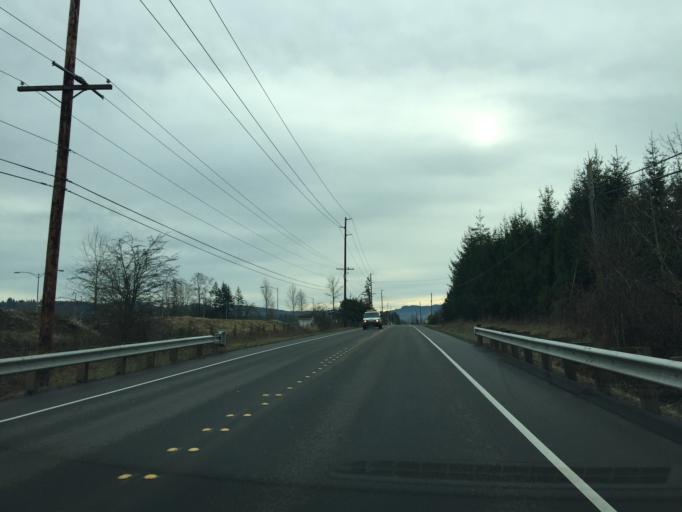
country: US
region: Washington
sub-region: Whatcom County
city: Bellingham
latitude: 48.7961
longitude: -122.4428
